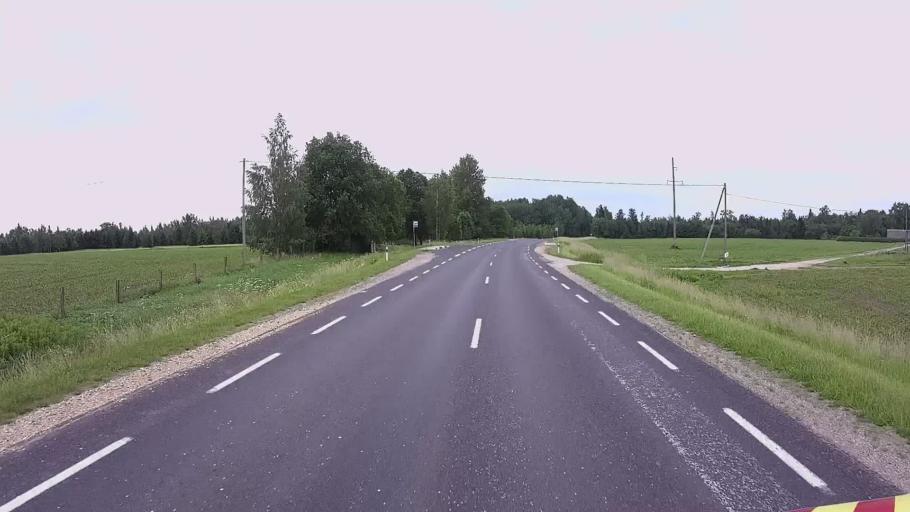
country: EE
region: Viljandimaa
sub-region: Karksi vald
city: Karksi-Nuia
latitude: 58.1981
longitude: 25.6156
